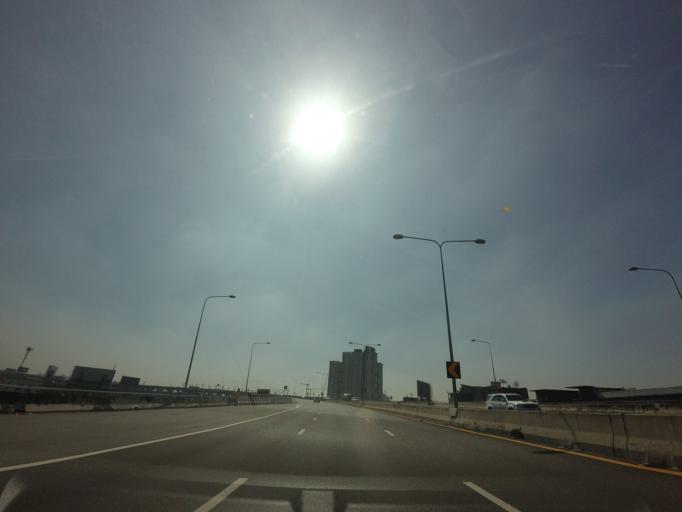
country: TH
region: Bangkok
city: Phra Khanong
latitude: 13.6766
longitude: 100.6043
